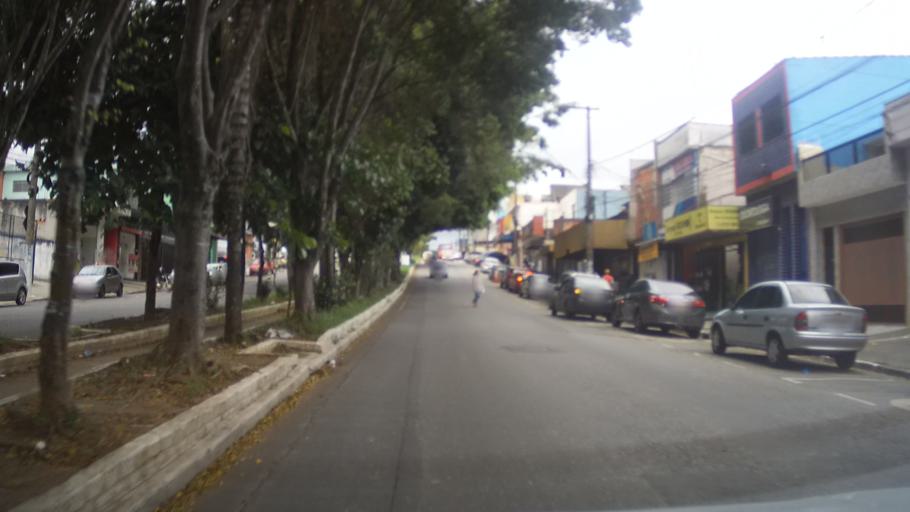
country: BR
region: Sao Paulo
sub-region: Aruja
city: Aruja
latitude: -23.4043
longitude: -46.4158
